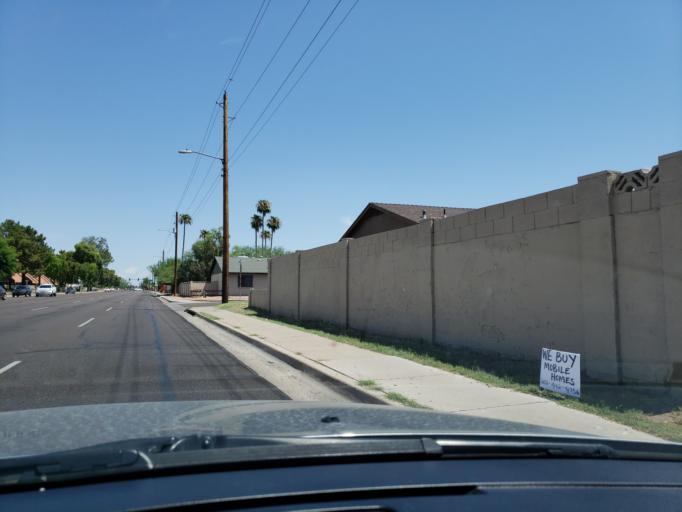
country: US
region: Arizona
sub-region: Maricopa County
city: Glendale
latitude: 33.5431
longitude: -112.1514
